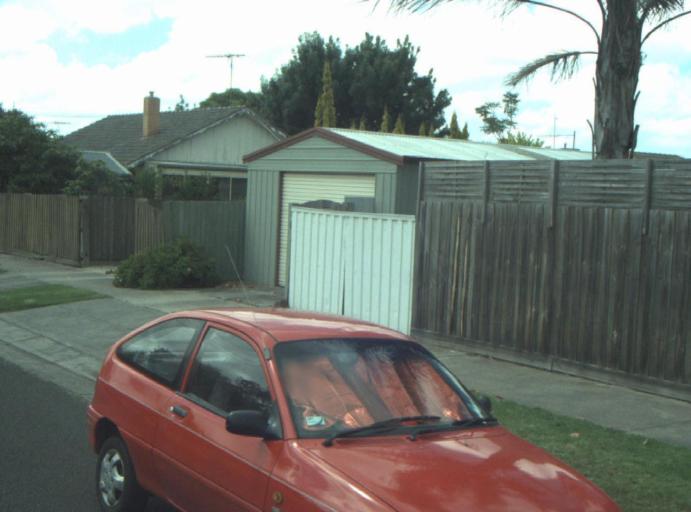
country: AU
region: Victoria
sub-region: Greater Geelong
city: Wandana Heights
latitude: -38.1751
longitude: 144.3323
